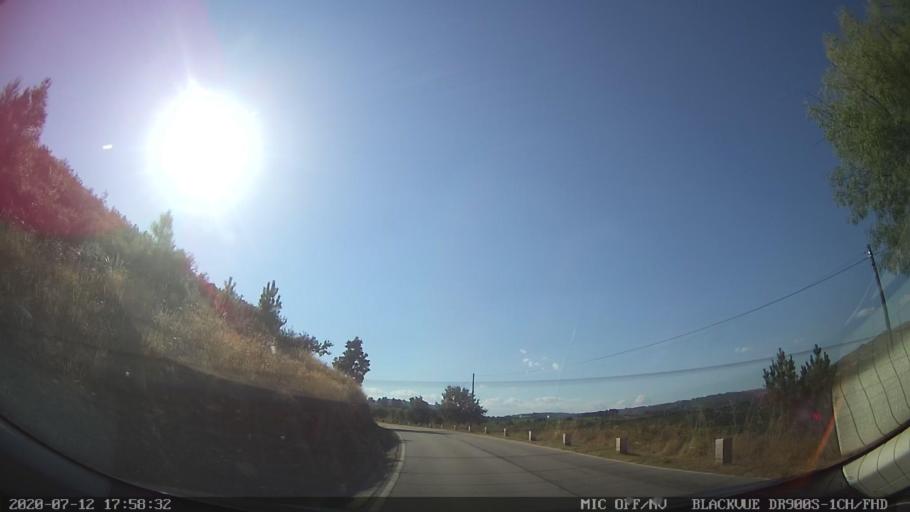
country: PT
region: Vila Real
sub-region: Sabrosa
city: Sabrosa
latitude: 41.2669
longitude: -7.4511
